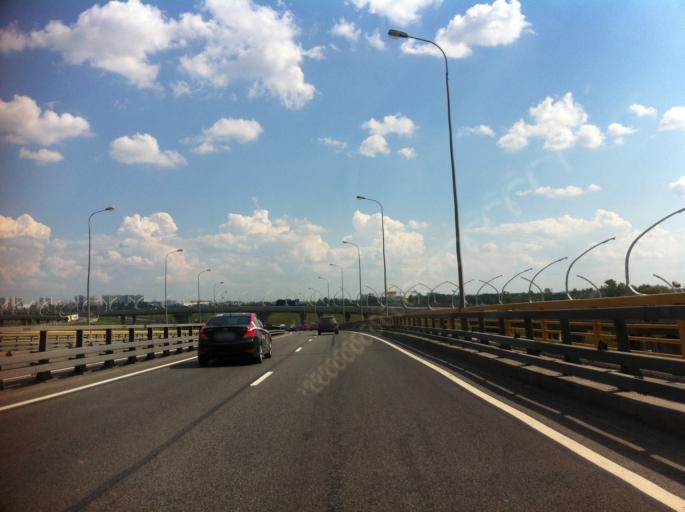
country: RU
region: St.-Petersburg
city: Dachnoye
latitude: 59.8347
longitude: 30.2688
